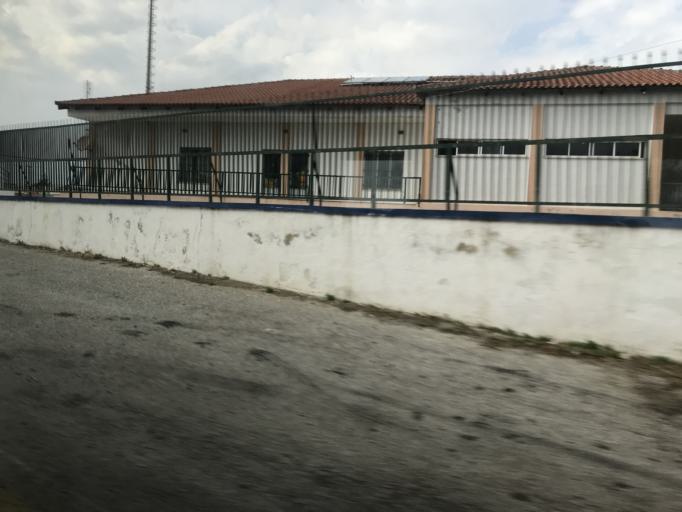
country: GR
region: East Macedonia and Thrace
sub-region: Nomos Rodopis
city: Sapes
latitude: 41.0267
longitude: 25.6886
